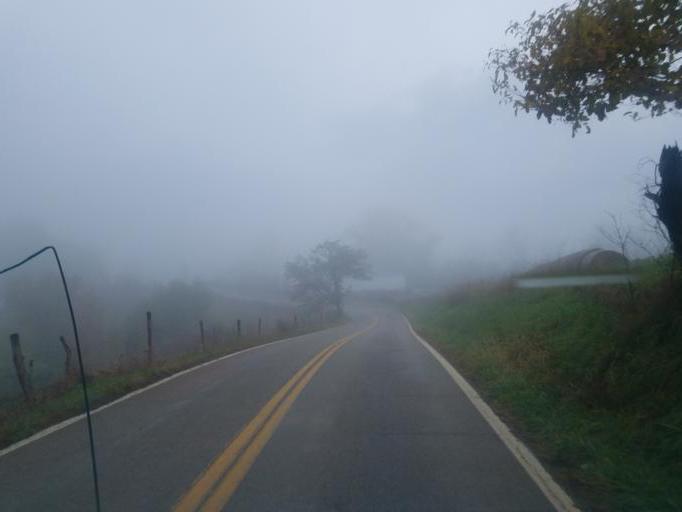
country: US
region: Ohio
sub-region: Morgan County
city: McConnelsville
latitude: 39.5181
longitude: -81.9306
